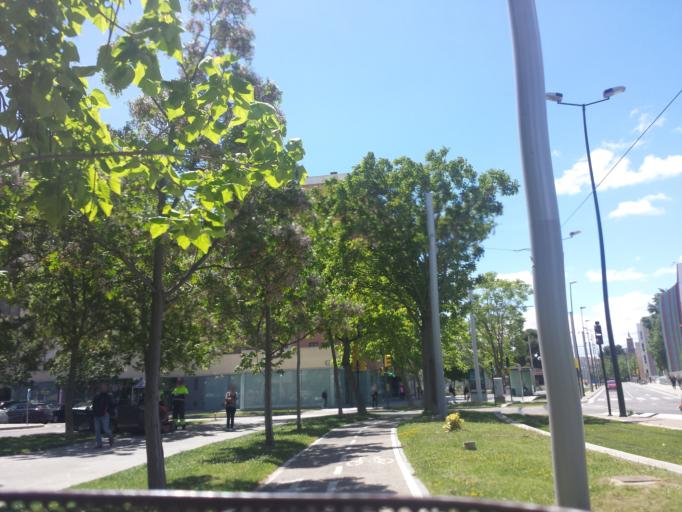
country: ES
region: Aragon
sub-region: Provincia de Zaragoza
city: Zaragoza
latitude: 41.6638
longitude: -0.8834
